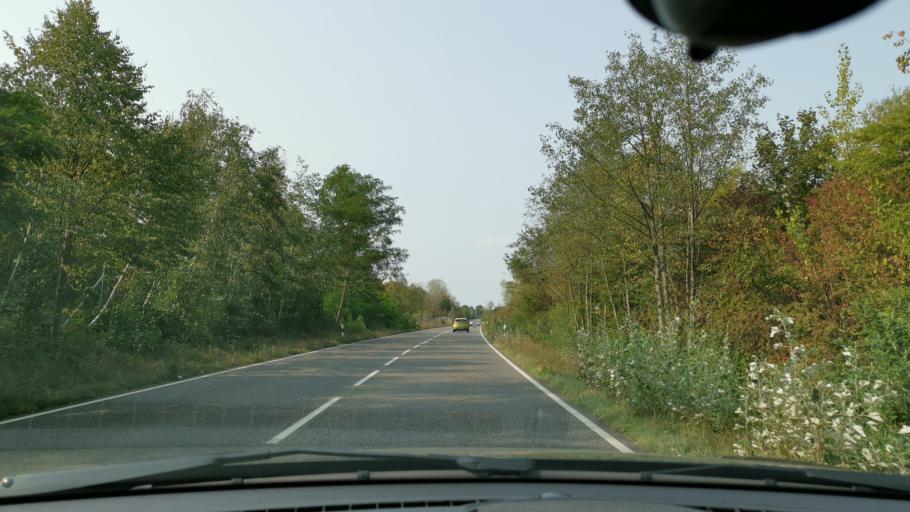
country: DE
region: North Rhine-Westphalia
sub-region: Regierungsbezirk Koln
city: Bergheim
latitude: 50.9727
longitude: 6.6063
